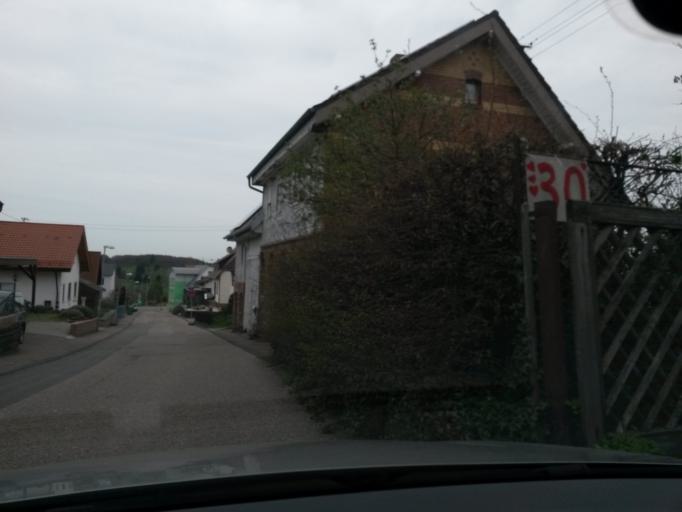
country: DE
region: Baden-Wuerttemberg
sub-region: Karlsruhe Region
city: Neuenburg
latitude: 48.8607
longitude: 8.5691
